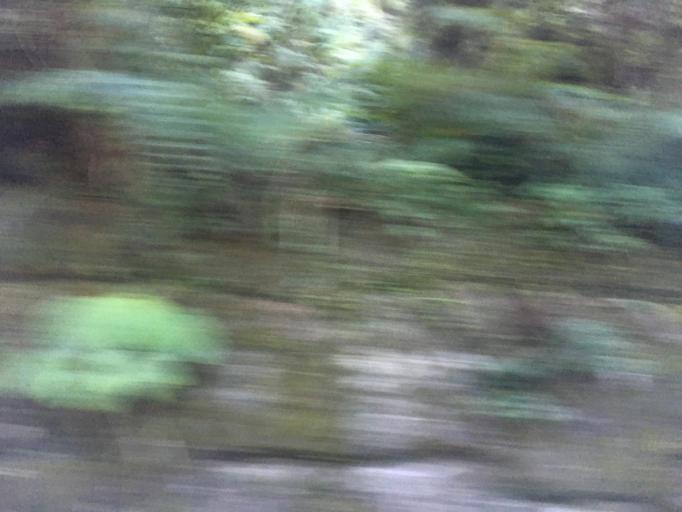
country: TW
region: Taiwan
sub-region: Yilan
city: Yilan
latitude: 24.5394
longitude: 121.5123
